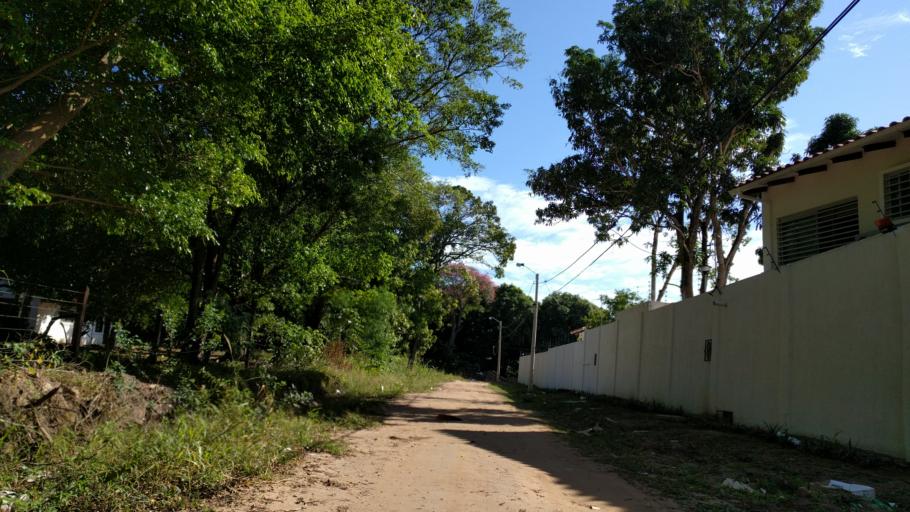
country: BO
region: Santa Cruz
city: Santa Cruz de la Sierra
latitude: -17.7987
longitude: -63.2212
